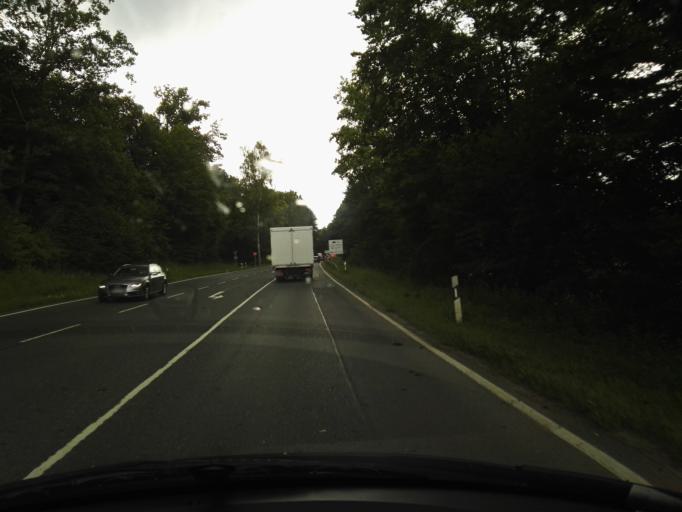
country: DE
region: Bavaria
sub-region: Upper Franconia
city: Michelau
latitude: 50.1514
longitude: 11.1258
